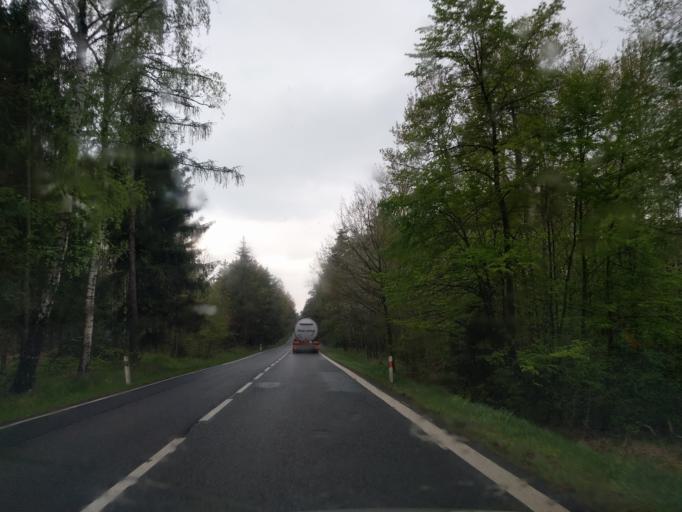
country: CZ
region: Central Bohemia
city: Dobris
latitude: 49.6947
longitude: 14.1796
